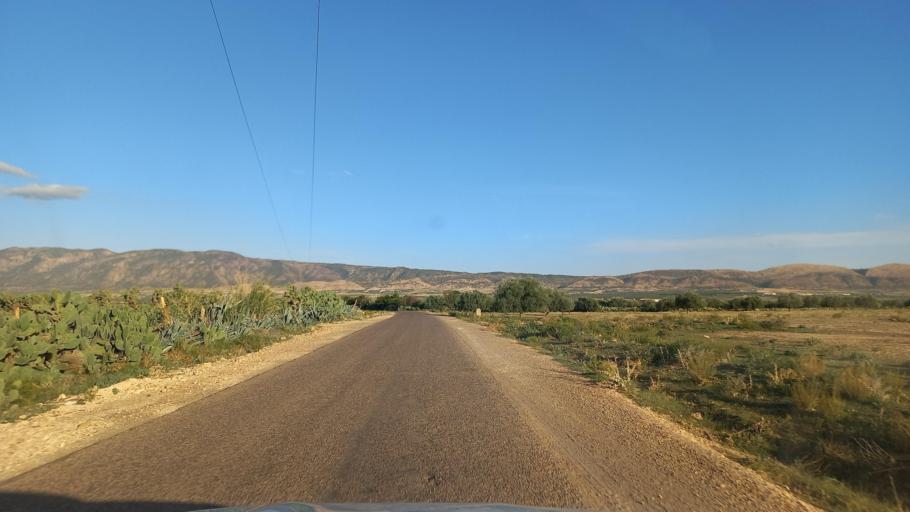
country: TN
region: Al Qasrayn
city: Sbiba
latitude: 35.4117
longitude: 9.1317
